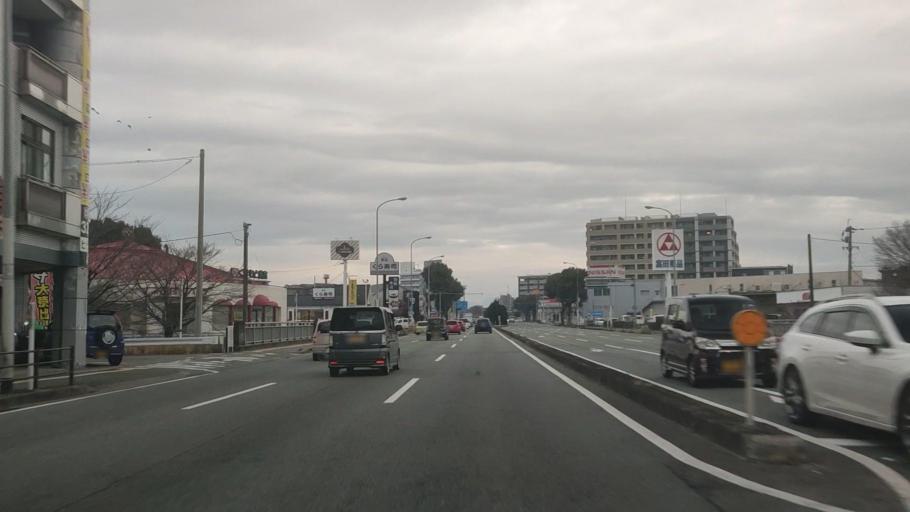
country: JP
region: Kumamoto
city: Kumamoto
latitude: 32.8111
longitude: 130.7492
